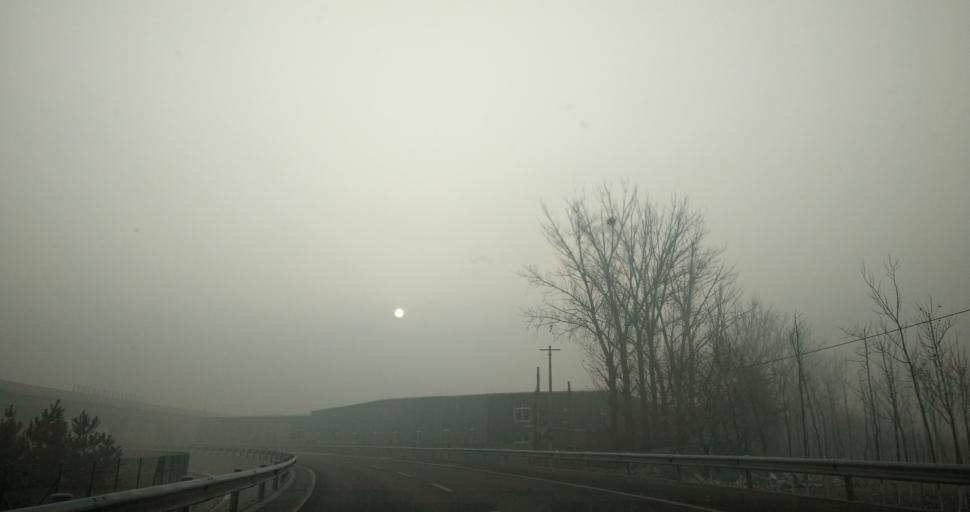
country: CN
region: Beijing
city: Yinghai
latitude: 39.7198
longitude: 116.4375
